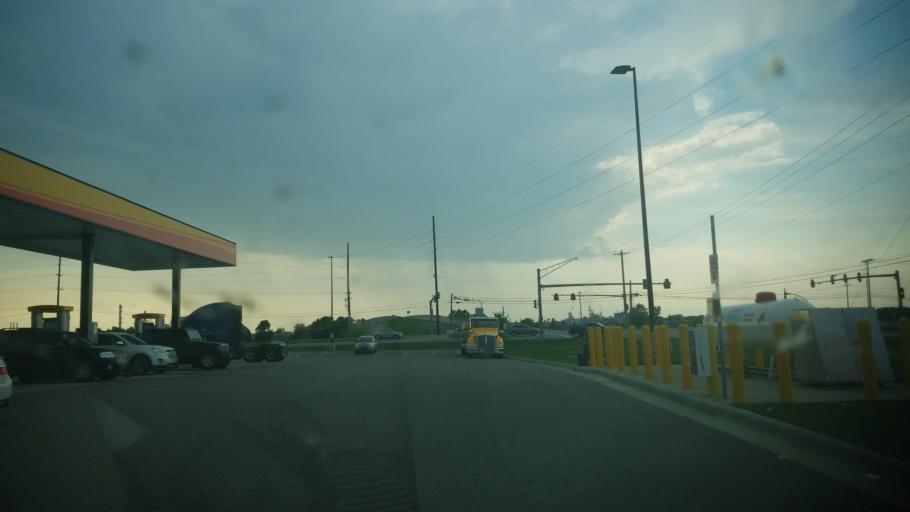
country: US
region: Ohio
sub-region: Pickaway County
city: Logan Elm Village
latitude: 39.5568
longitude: -82.9577
